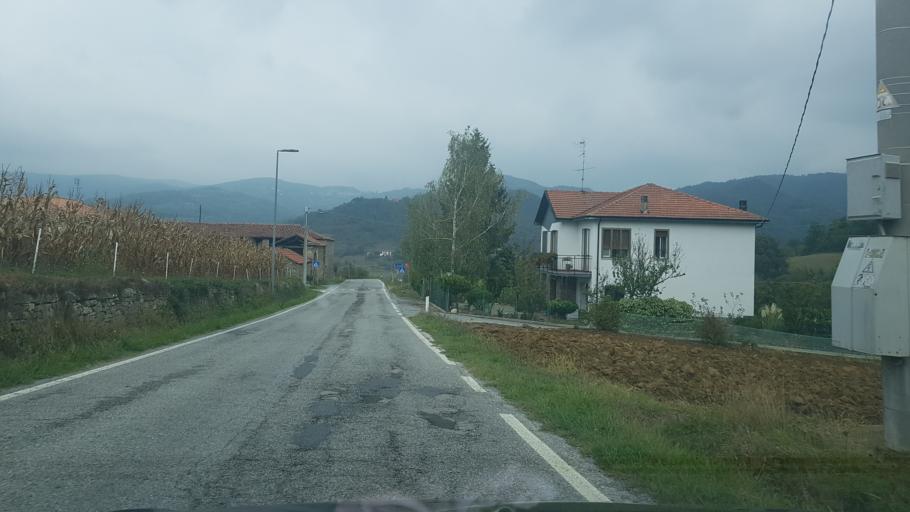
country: IT
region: Piedmont
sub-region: Provincia di Cuneo
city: Camerana
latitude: 44.4308
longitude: 8.1470
